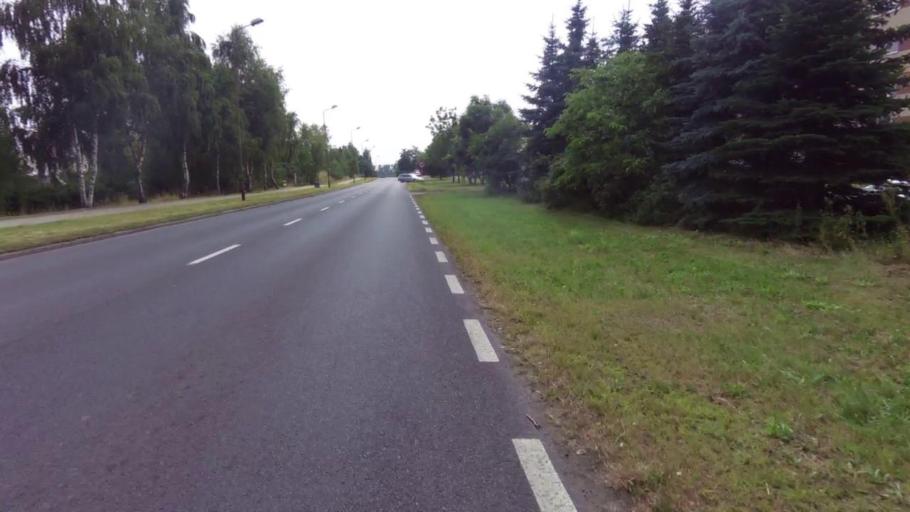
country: PL
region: West Pomeranian Voivodeship
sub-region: Powiat choszczenski
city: Choszczno
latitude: 53.1769
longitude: 15.4108
